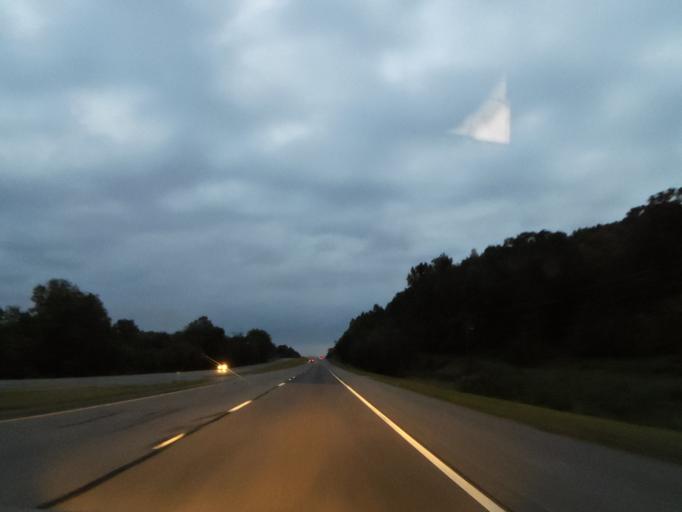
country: US
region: Alabama
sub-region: Madison County
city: New Hope
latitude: 34.6490
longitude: -86.3246
